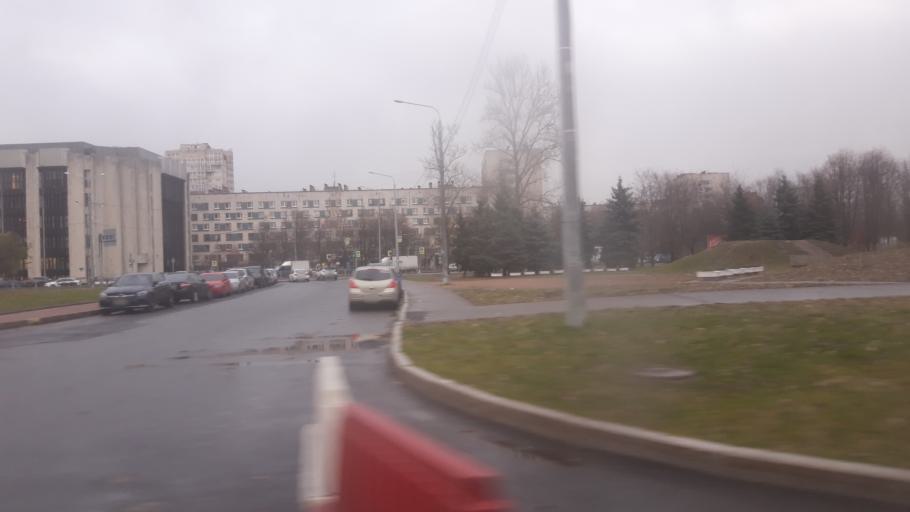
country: RU
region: St.-Petersburg
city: Kupchino
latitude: 59.8415
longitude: 30.3224
